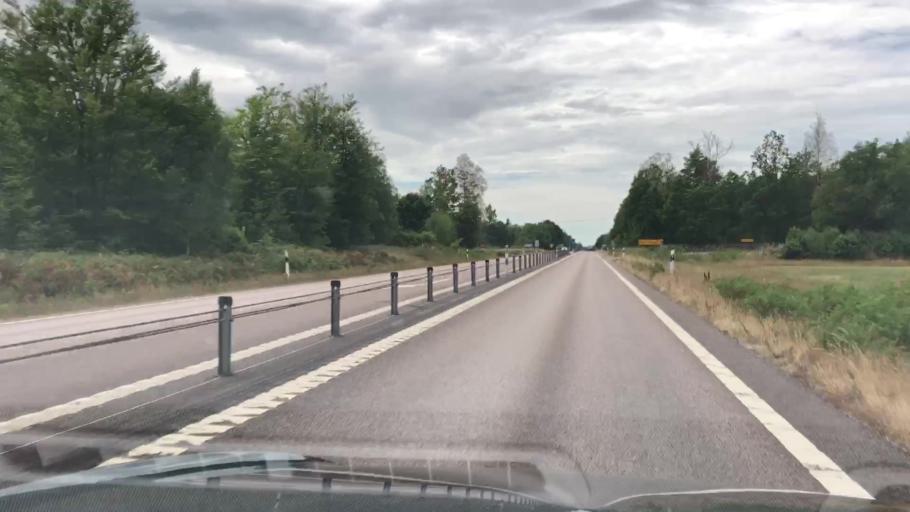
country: SE
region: Kalmar
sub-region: Torsas Kommun
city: Torsas
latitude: 56.2762
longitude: 15.9705
